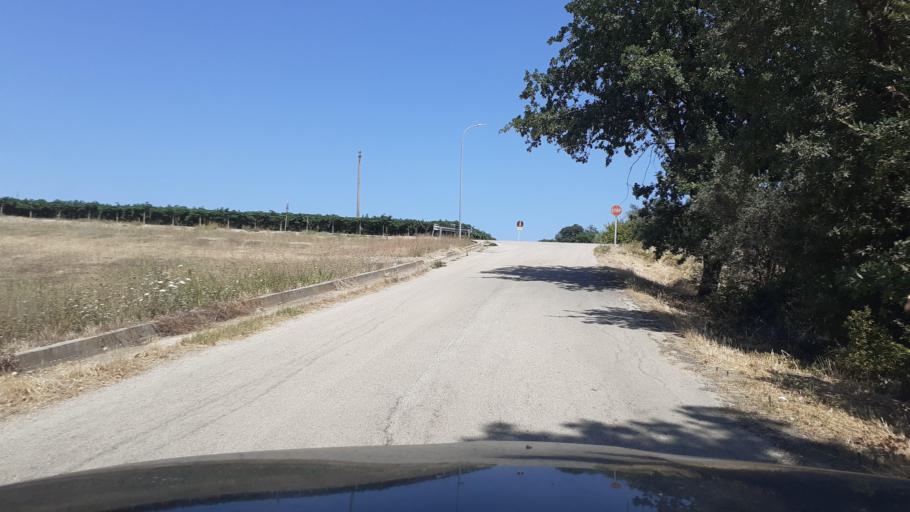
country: IT
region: Abruzzo
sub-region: Provincia di Chieti
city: Santa Maria Imbaro
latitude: 42.2147
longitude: 14.4651
